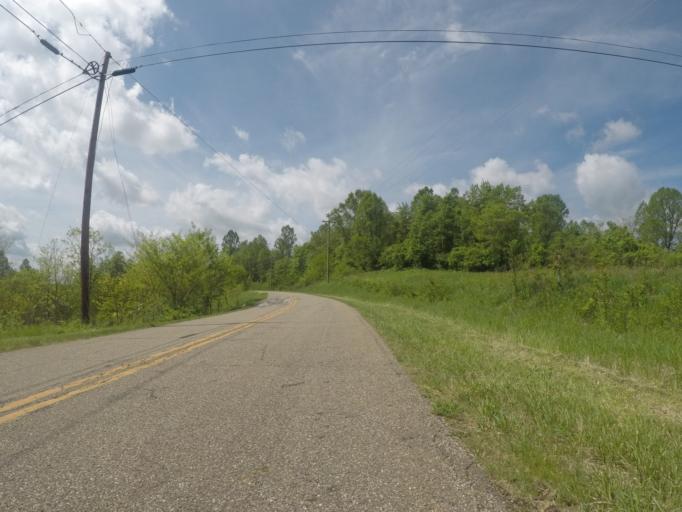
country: US
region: West Virginia
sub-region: Cabell County
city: Huntington
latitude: 38.5434
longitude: -82.4318
